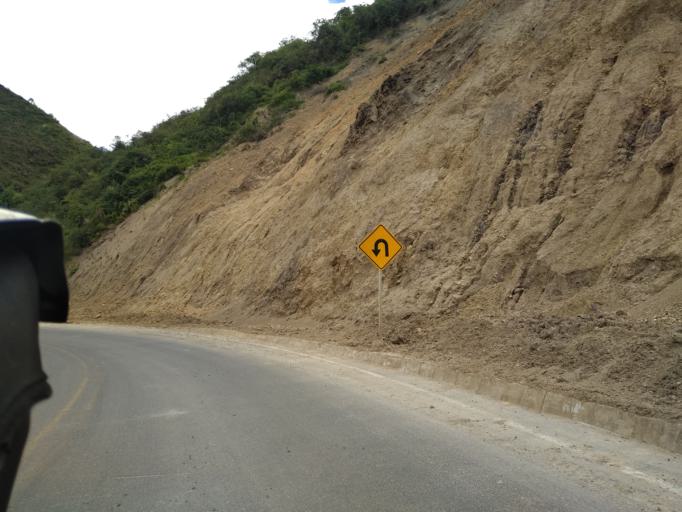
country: EC
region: Cotopaxi
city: Saquisili
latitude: -0.7519
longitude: -78.9118
